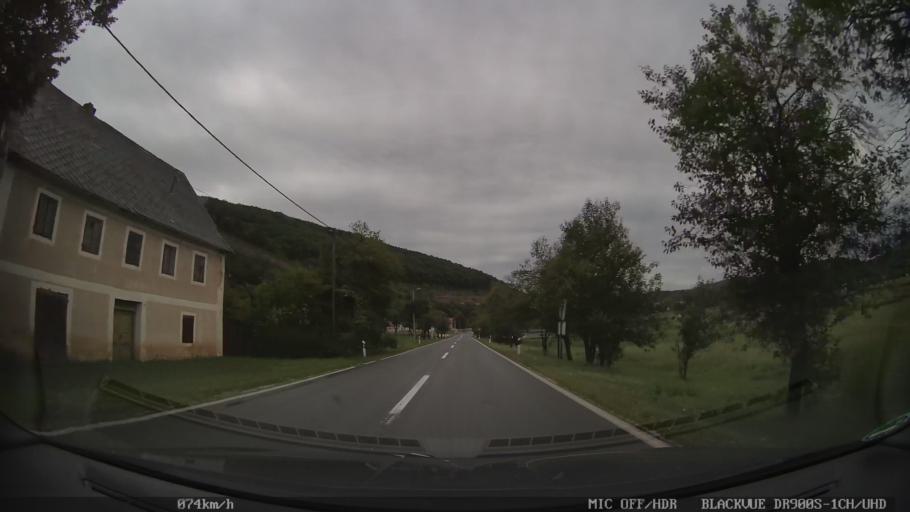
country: HR
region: Licko-Senjska
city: Otocac
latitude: 44.9017
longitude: 15.1786
